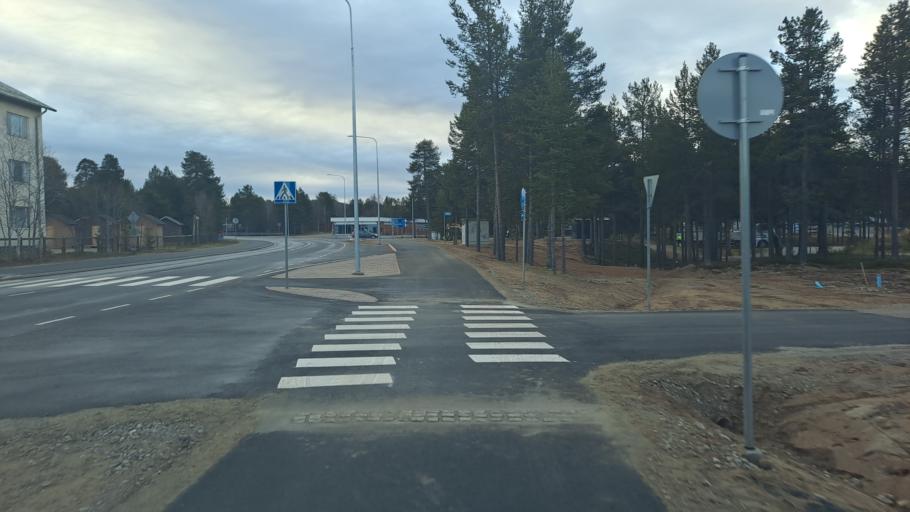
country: FI
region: Lapland
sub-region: Pohjois-Lappi
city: Inari
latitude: 68.9079
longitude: 27.0143
